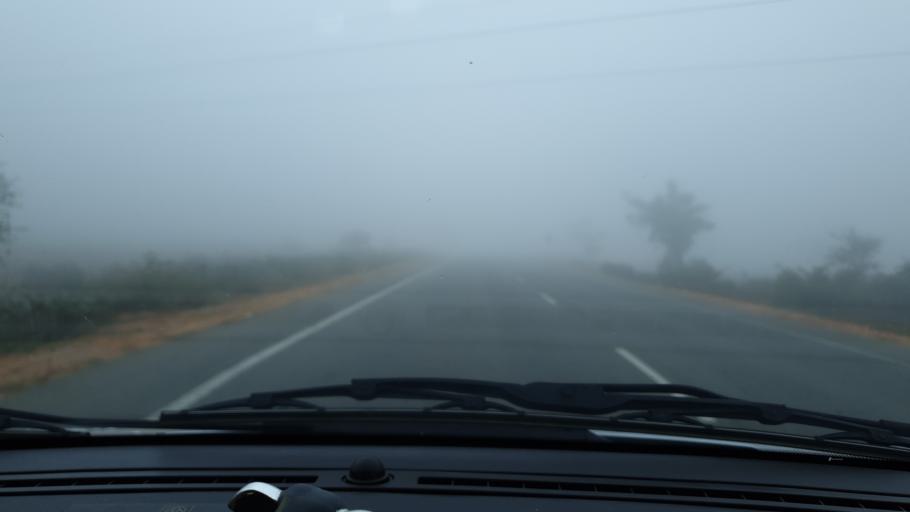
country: IN
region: Telangana
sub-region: Mahbubnagar
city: Nagar Karnul
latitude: 16.6761
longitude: 78.5292
